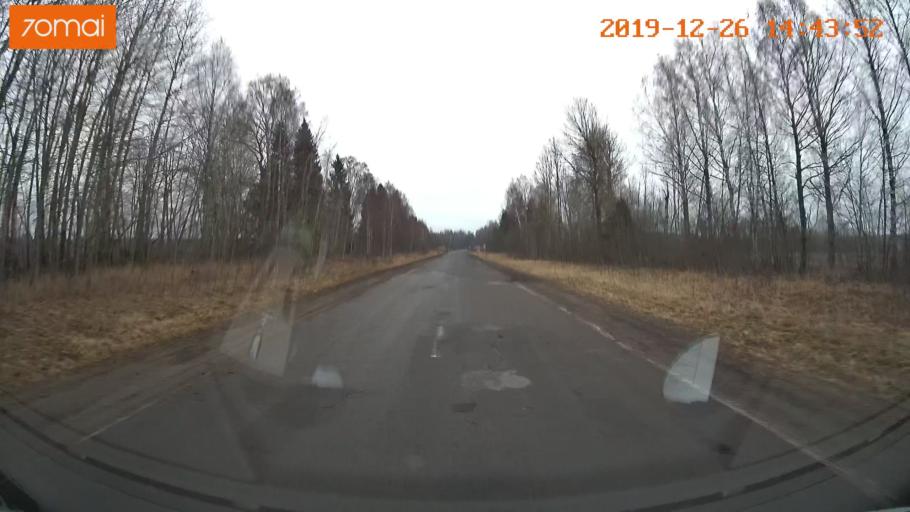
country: RU
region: Jaroslavl
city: Poshekhon'ye
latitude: 58.3529
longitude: 39.0450
